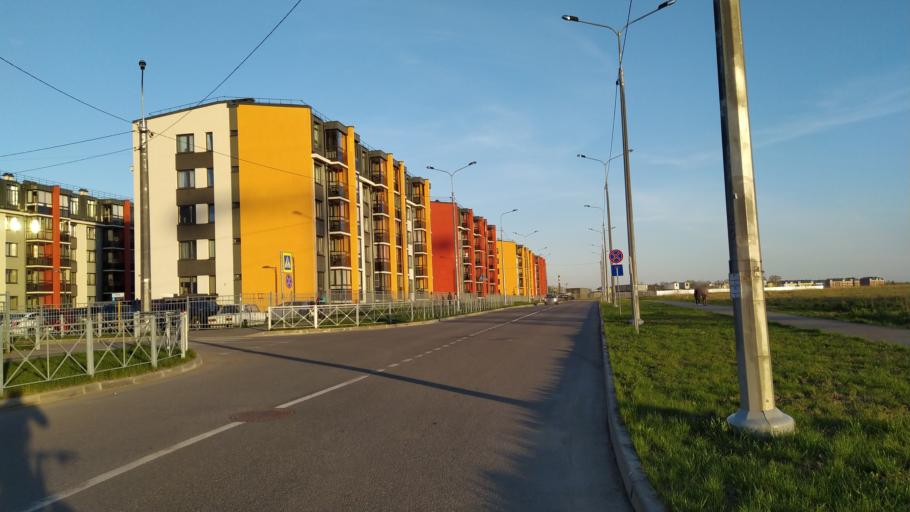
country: RU
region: St.-Petersburg
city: Pushkin
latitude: 59.6986
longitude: 30.4044
